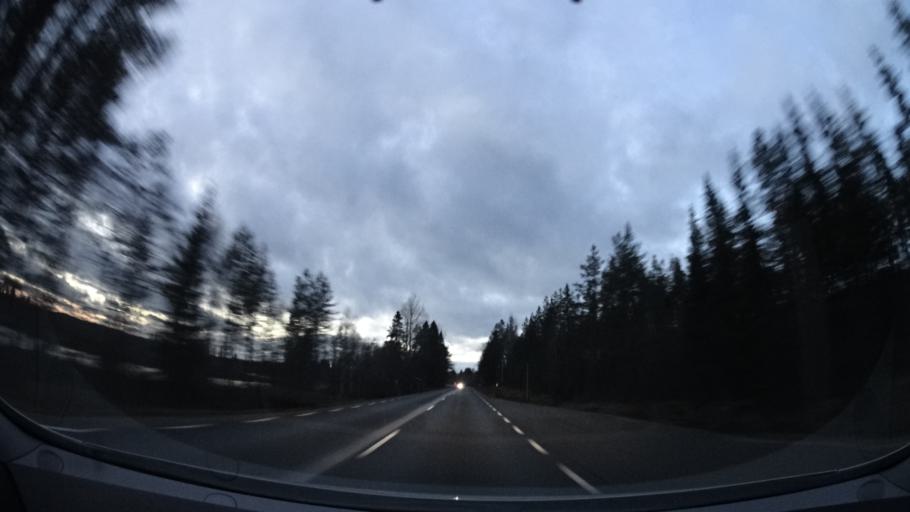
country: SE
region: Vaesterbotten
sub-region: Asele Kommun
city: Asele
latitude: 64.1867
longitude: 17.1781
